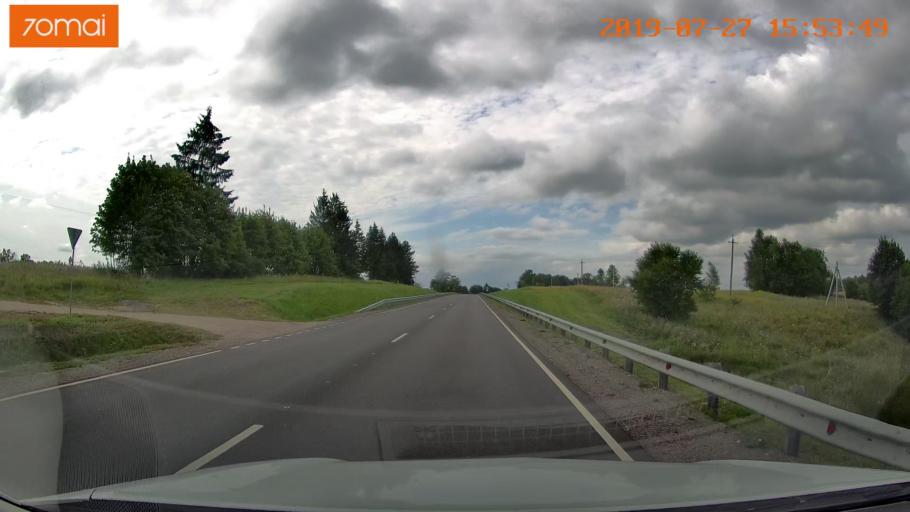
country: RU
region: Kaliningrad
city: Chernyakhovsk
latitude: 54.6049
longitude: 21.9479
